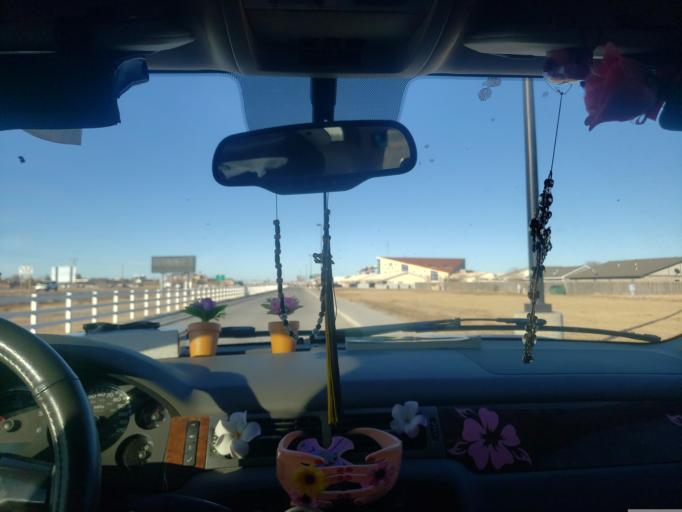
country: US
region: Kansas
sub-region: Finney County
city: Garden City
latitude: 37.9695
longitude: -100.8385
